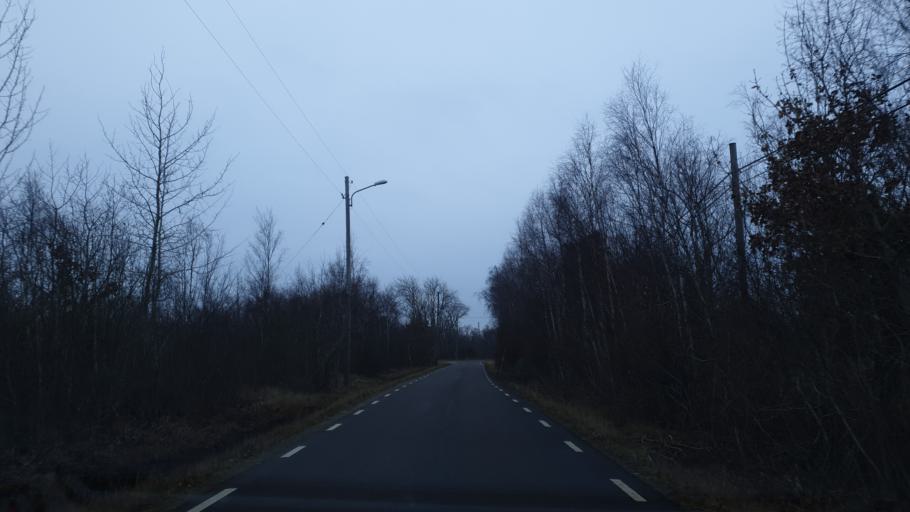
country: SE
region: Blekinge
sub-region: Karlskrona Kommun
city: Karlskrona
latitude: 56.1213
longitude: 15.6234
